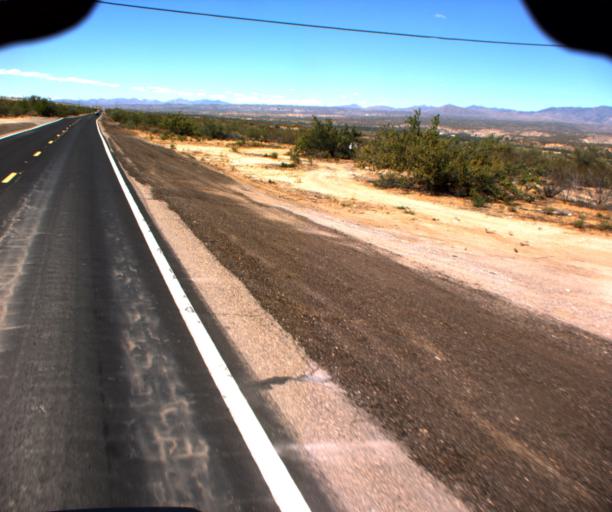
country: US
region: Arizona
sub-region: Yavapai County
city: Bagdad
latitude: 34.7196
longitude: -113.6148
